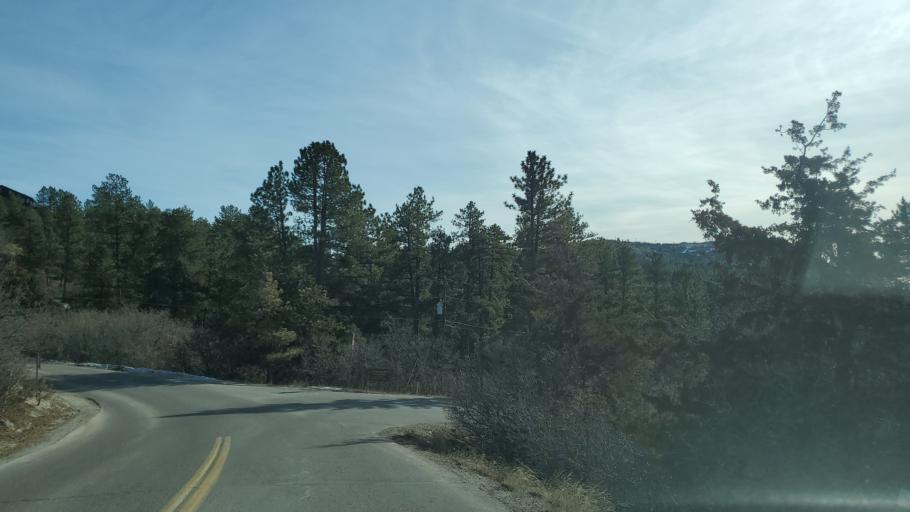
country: US
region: Colorado
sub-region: Douglas County
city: Castle Pines
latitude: 39.4367
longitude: -104.8750
